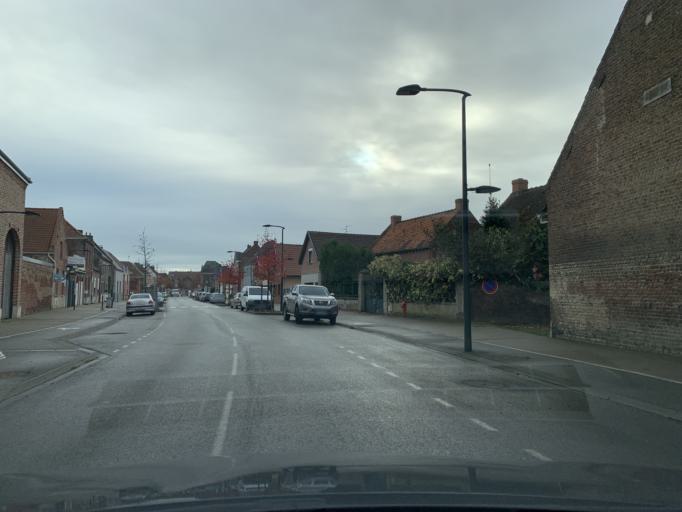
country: FR
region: Nord-Pas-de-Calais
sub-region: Departement du Nord
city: Cantin
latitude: 50.3115
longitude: 3.1241
